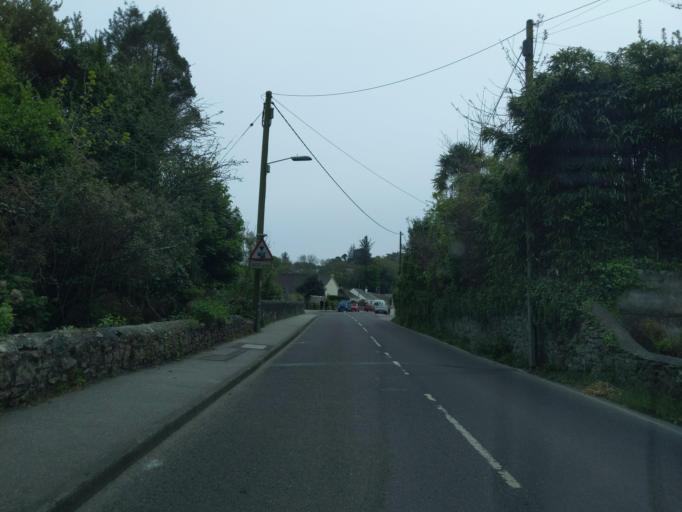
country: GB
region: England
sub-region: Cornwall
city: Par
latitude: 50.3528
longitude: -4.7106
